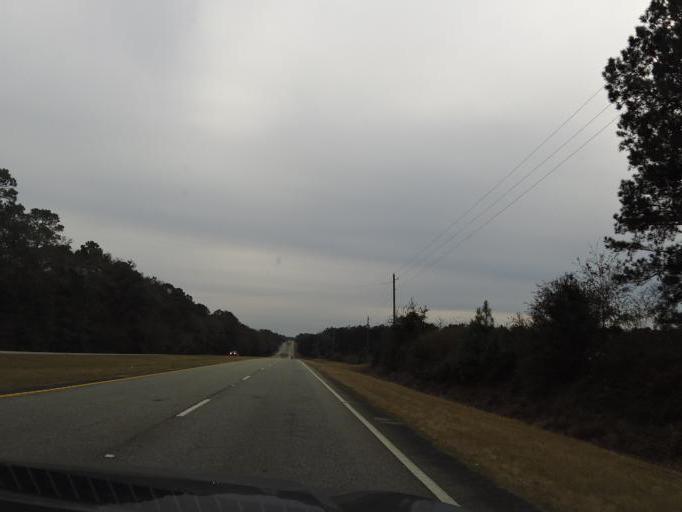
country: US
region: Georgia
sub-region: Thomas County
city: Boston
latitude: 30.7265
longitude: -83.8982
